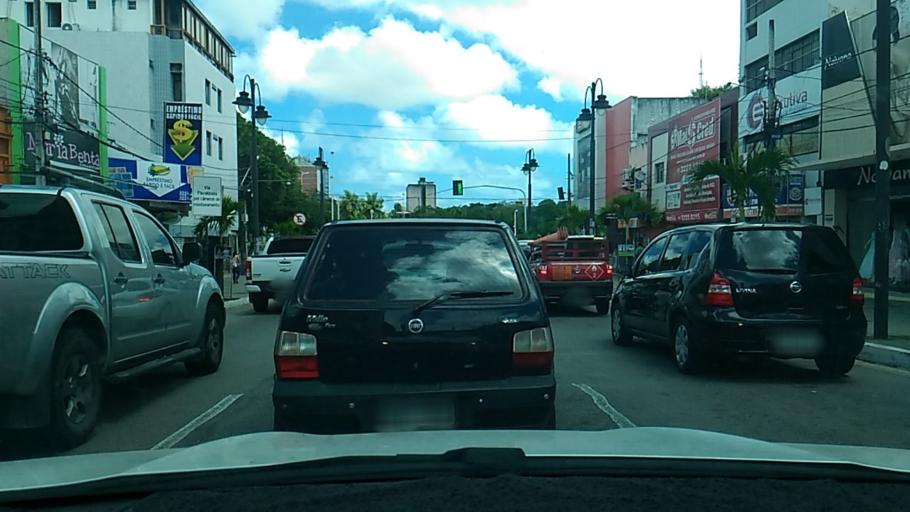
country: BR
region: Paraiba
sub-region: Joao Pessoa
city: Joao Pessoa
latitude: -7.1198
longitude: -34.8826
